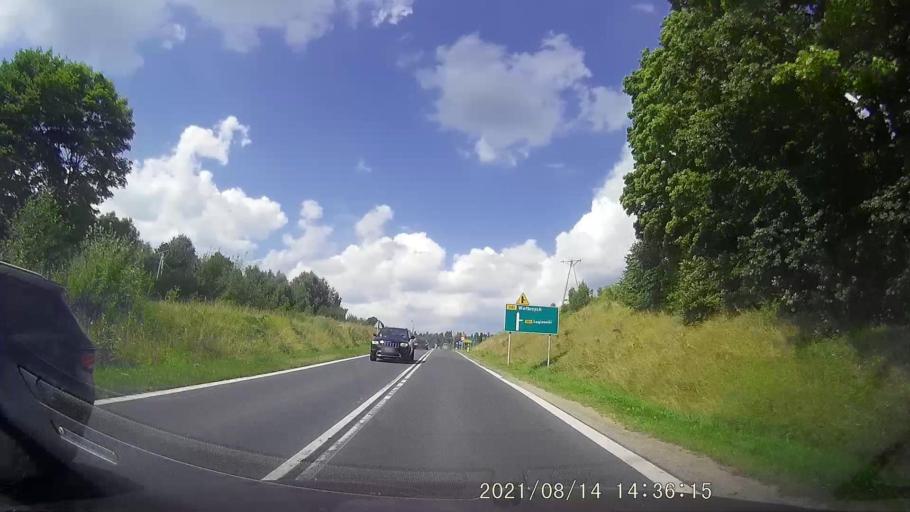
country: PL
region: Lower Silesian Voivodeship
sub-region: Powiat klodzki
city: Nowa Ruda
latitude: 50.5800
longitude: 16.5265
